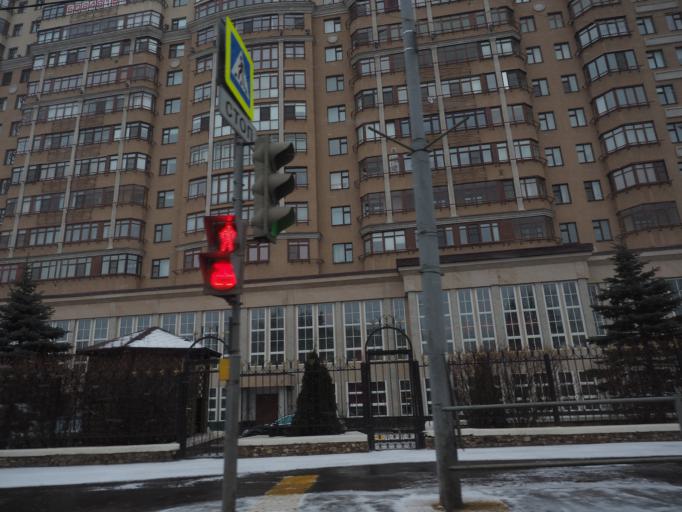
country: RU
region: Moscow
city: Vorob'yovo
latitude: 55.7138
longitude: 37.5241
